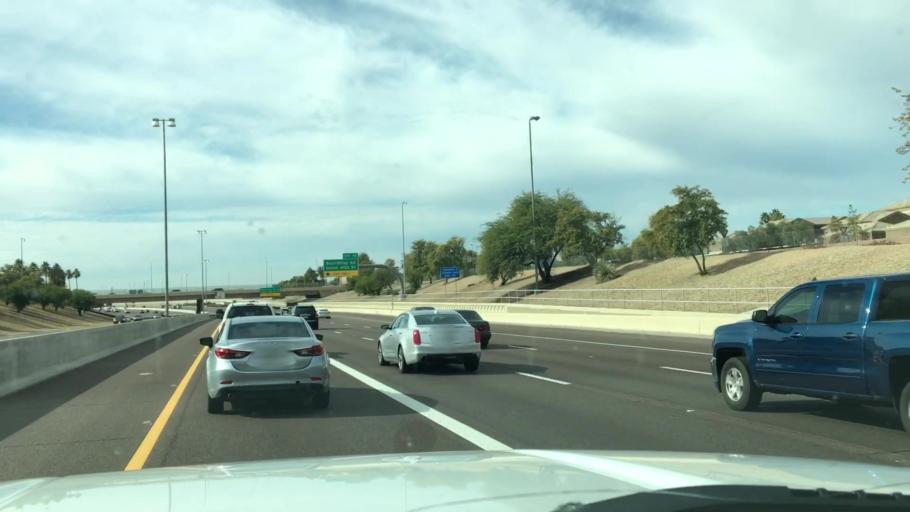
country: US
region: Arizona
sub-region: Maricopa County
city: Sun City
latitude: 33.6662
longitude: -112.2169
